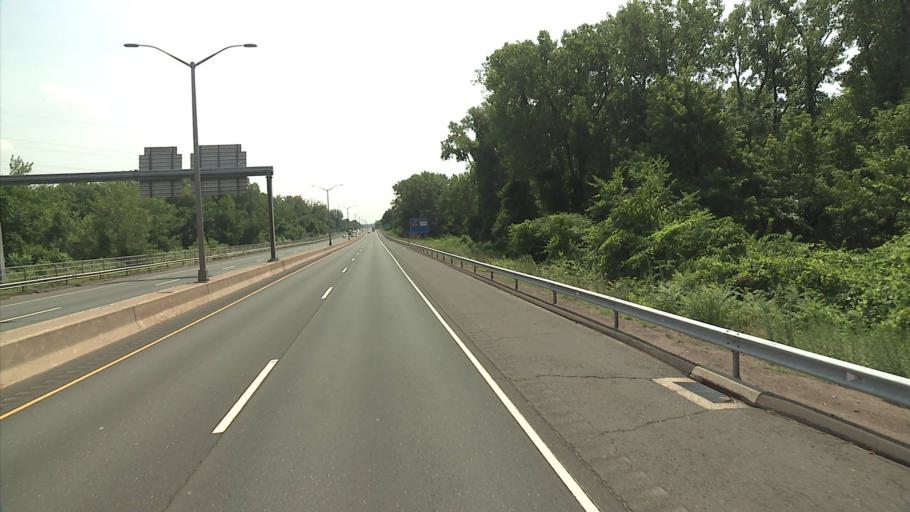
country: US
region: Connecticut
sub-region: Hartford County
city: South Windsor
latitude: 41.8099
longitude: -72.6323
